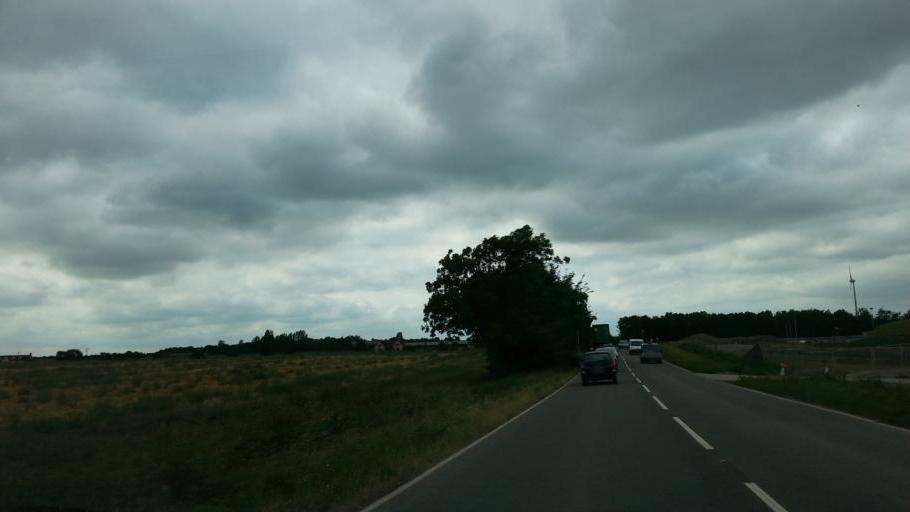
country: GB
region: England
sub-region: Cambridgeshire
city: Godmanchester
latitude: 52.2926
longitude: -0.1498
